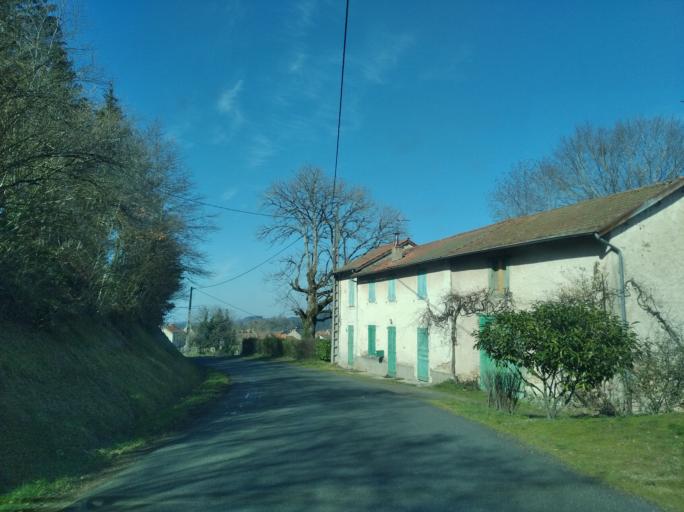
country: FR
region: Auvergne
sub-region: Departement de l'Allier
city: Le Mayet-de-Montagne
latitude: 46.1117
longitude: 3.6862
